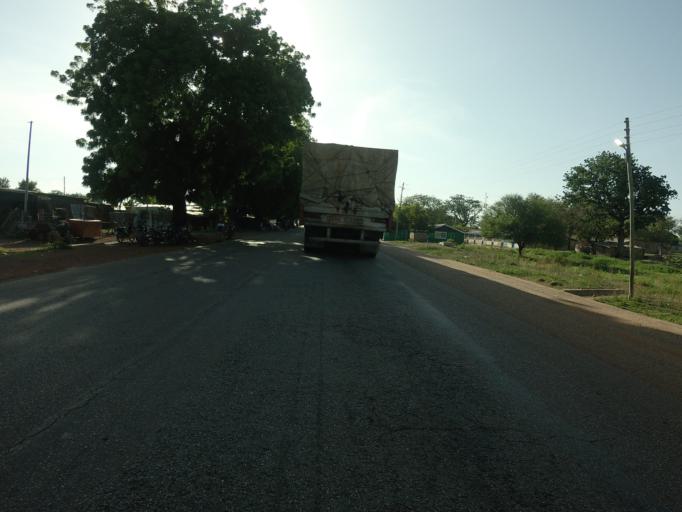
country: GH
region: Upper East
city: Navrongo
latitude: 10.8935
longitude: -1.0817
